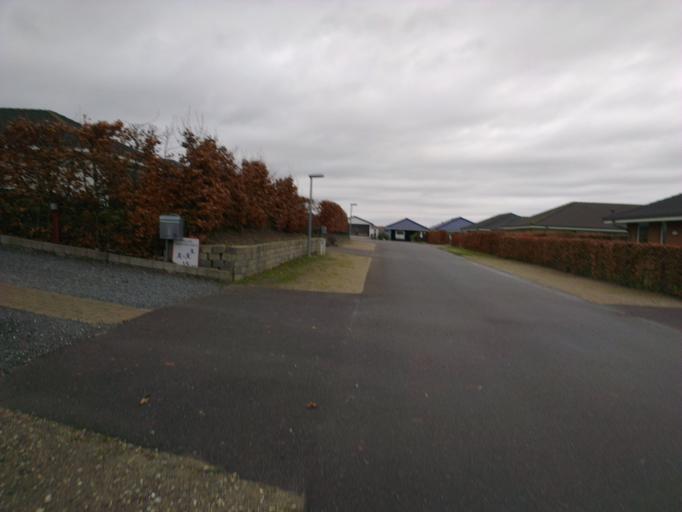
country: DK
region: Capital Region
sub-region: Frederikssund Kommune
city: Jaegerspris
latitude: 55.8369
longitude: 11.9911
